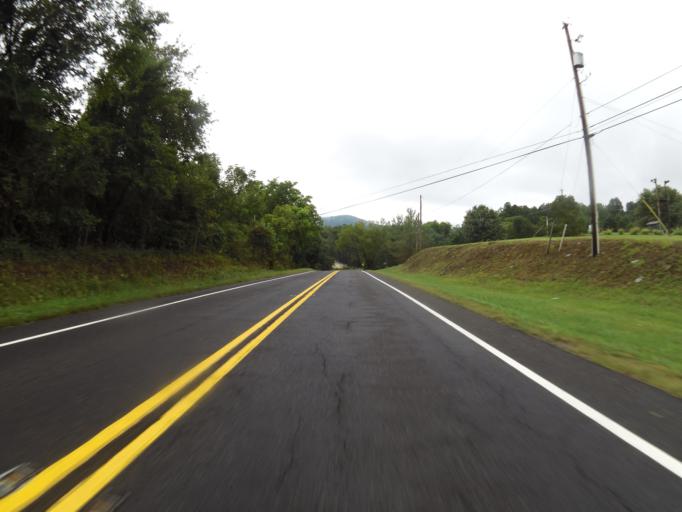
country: US
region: Virginia
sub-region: Rappahannock County
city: Washington
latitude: 38.6563
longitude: -78.2384
